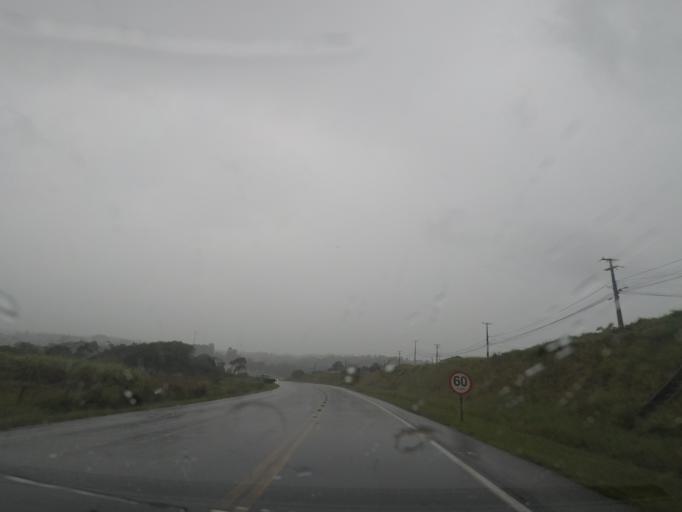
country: BR
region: Parana
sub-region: Almirante Tamandare
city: Almirante Tamandare
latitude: -25.3538
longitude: -49.2859
